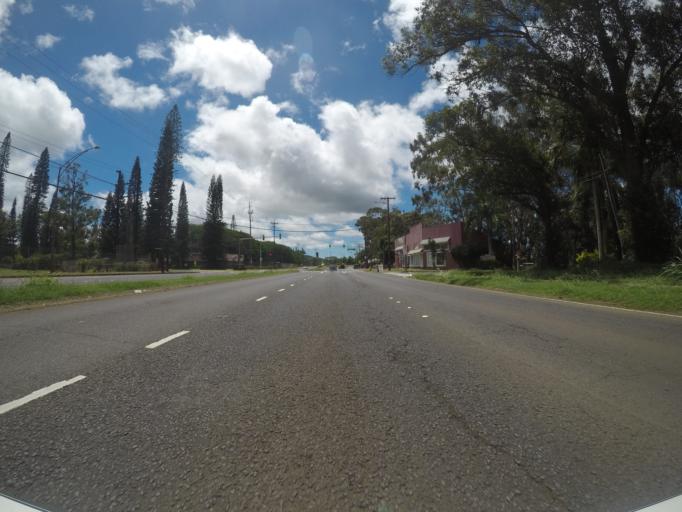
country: US
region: Hawaii
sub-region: Honolulu County
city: Schofield Barracks
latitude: 21.4932
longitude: -158.0484
